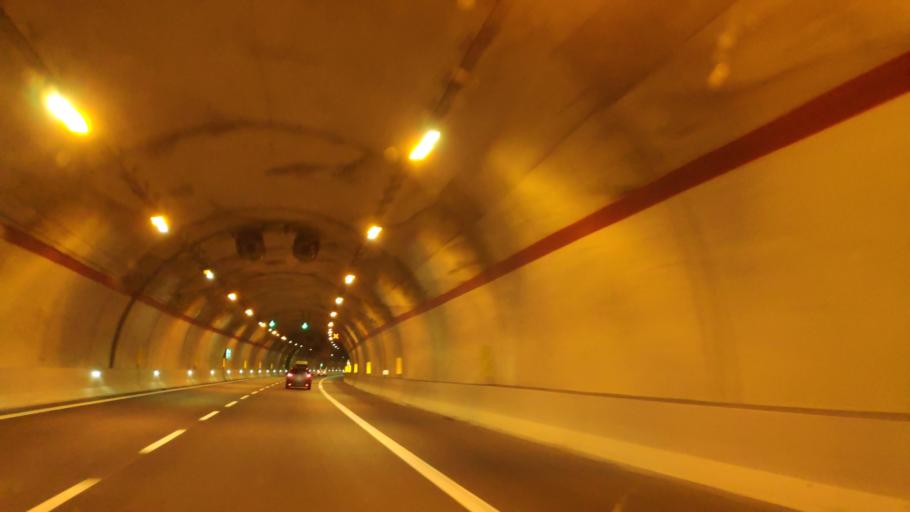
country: IT
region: Calabria
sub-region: Provincia di Cosenza
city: Mormanno
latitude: 39.8817
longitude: 15.9842
